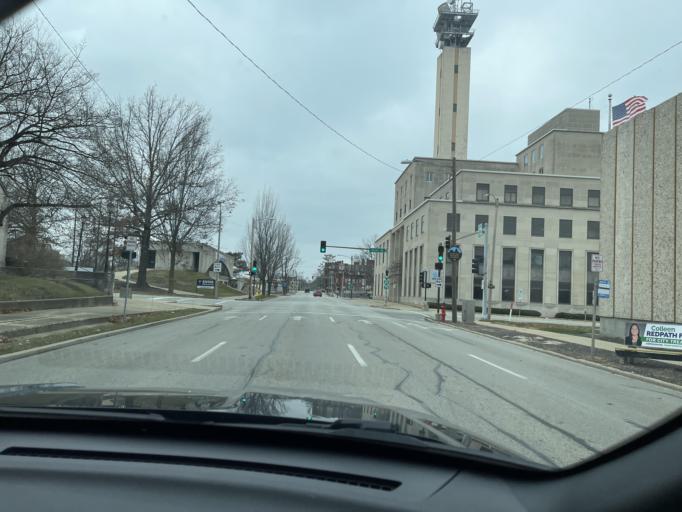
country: US
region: Illinois
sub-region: Sangamon County
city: Springfield
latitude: 39.7949
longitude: -89.6475
